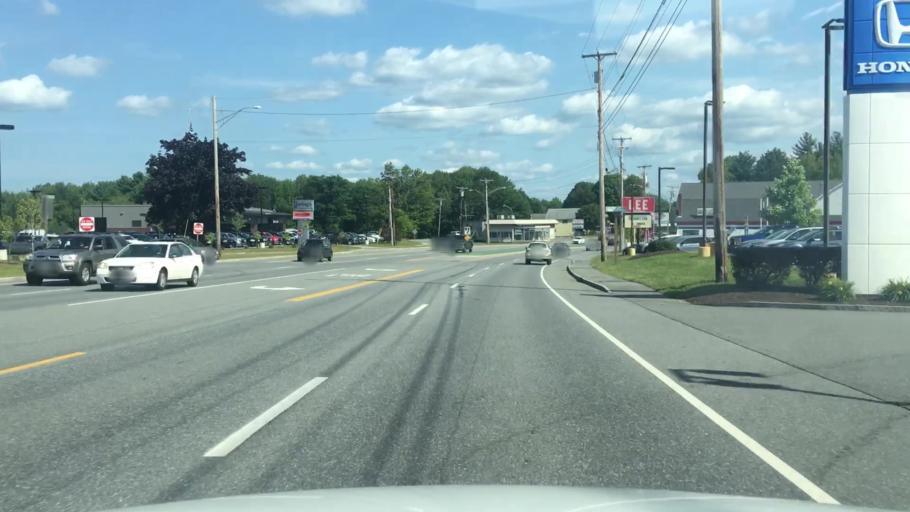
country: US
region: Maine
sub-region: Kennebec County
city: Manchester
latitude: 44.3195
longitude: -69.8209
